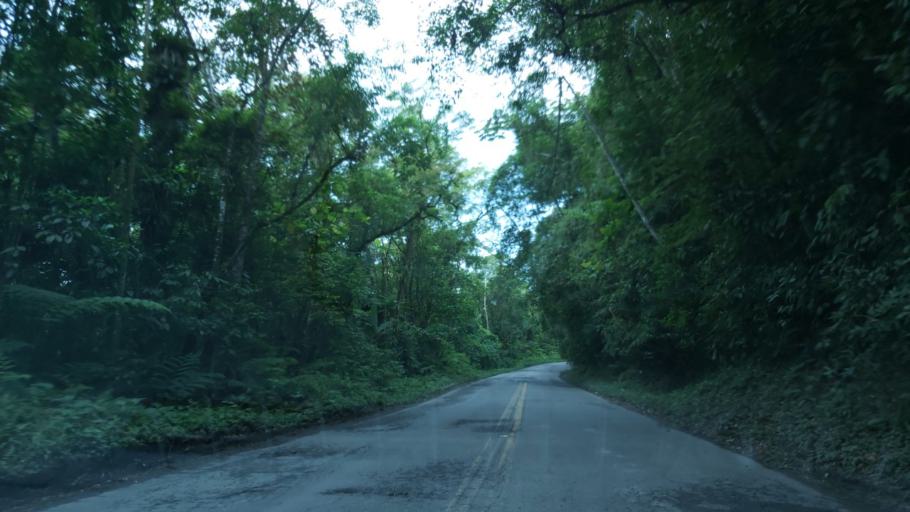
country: BR
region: Sao Paulo
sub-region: Miracatu
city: Miracatu
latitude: -24.0371
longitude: -47.5668
